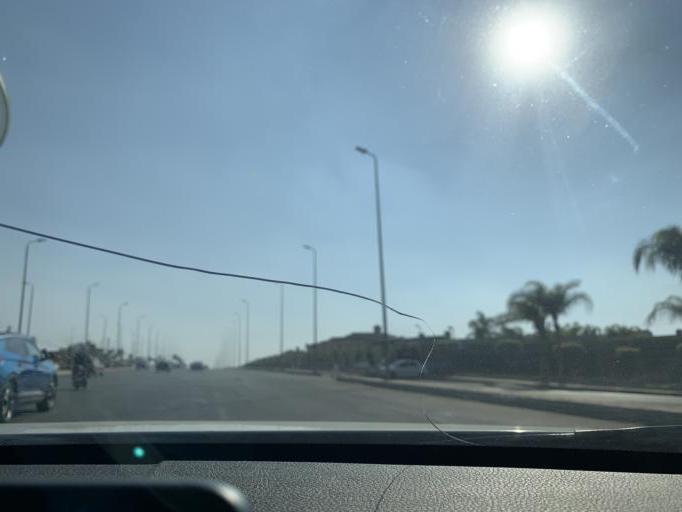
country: EG
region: Muhafazat al Qalyubiyah
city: Al Khankah
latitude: 30.0207
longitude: 31.4747
